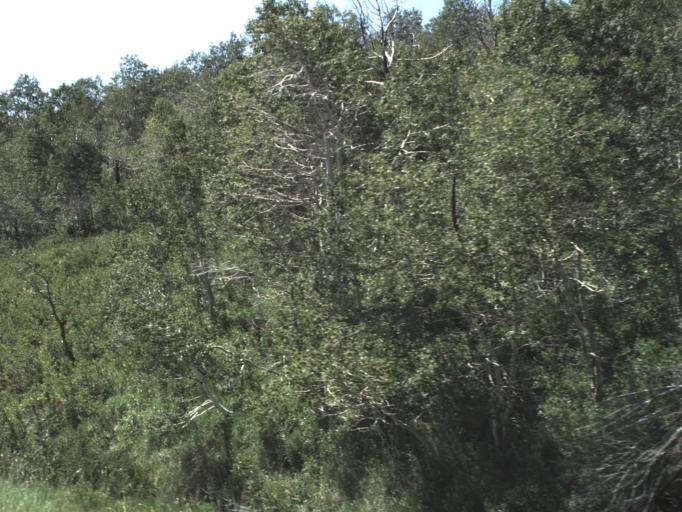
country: US
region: Utah
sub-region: Weber County
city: Wolf Creek
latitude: 41.4052
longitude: -111.5478
